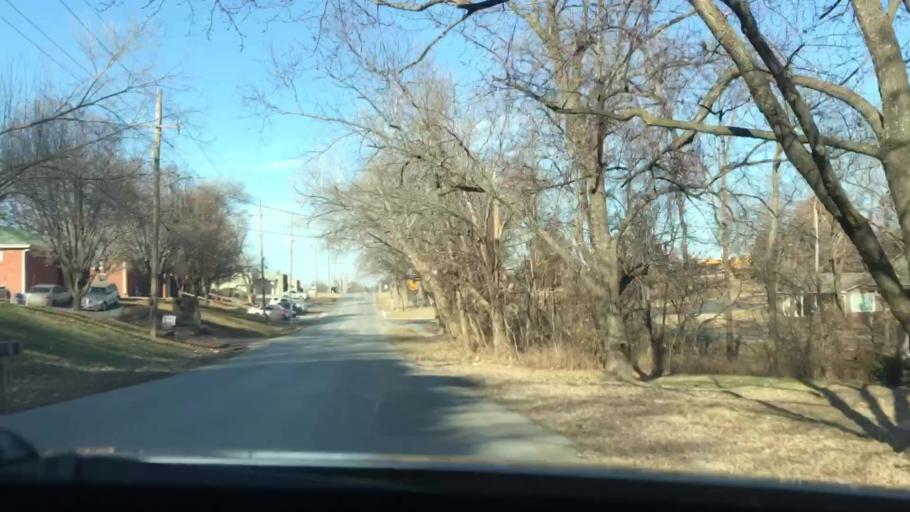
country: US
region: Missouri
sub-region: Platte County
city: Parkville
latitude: 39.2063
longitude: -94.6871
